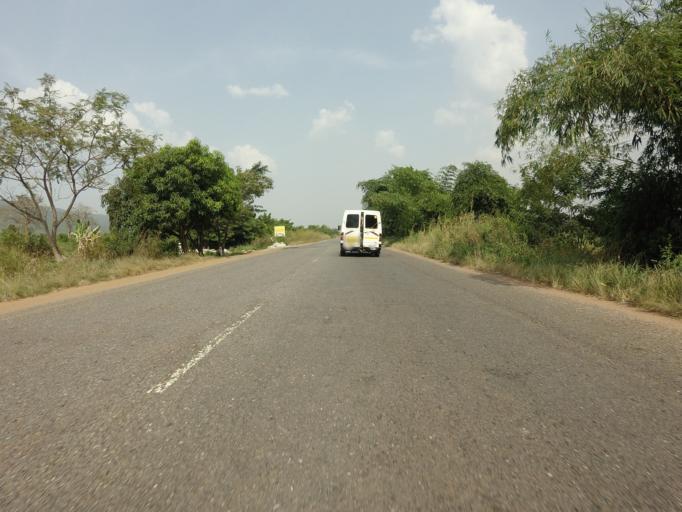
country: GH
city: Akropong
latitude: 5.9330
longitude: -0.0354
